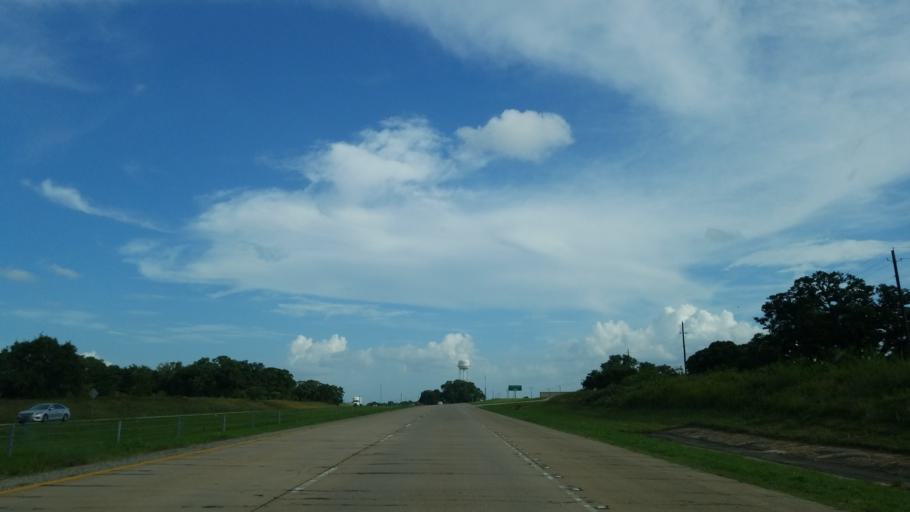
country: US
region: Texas
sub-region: Colorado County
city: Columbus
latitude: 29.7148
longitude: -96.5797
